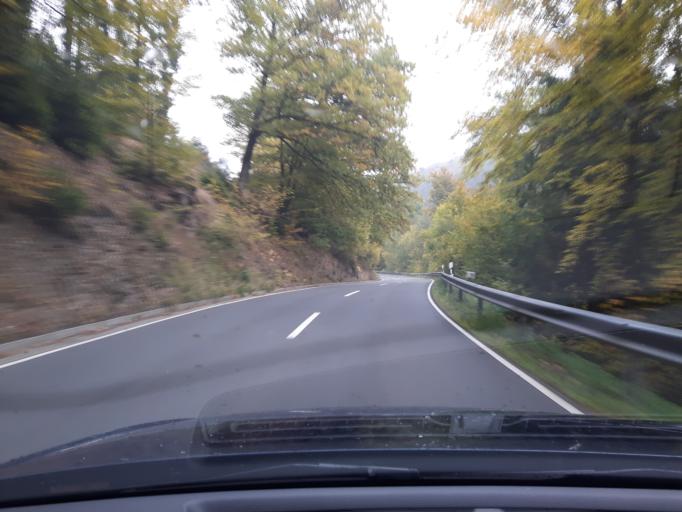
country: DE
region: North Rhine-Westphalia
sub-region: Regierungsbezirk Arnsberg
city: Bad Laasphe
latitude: 50.9503
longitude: 8.3954
